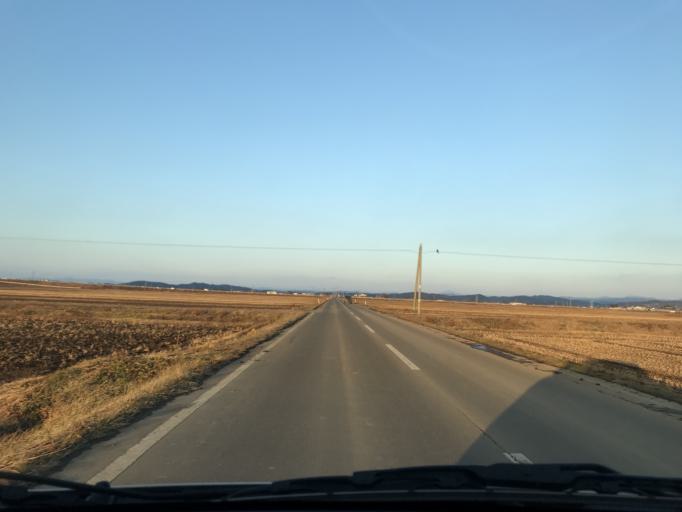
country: JP
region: Miyagi
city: Wakuya
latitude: 38.7134
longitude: 141.1560
